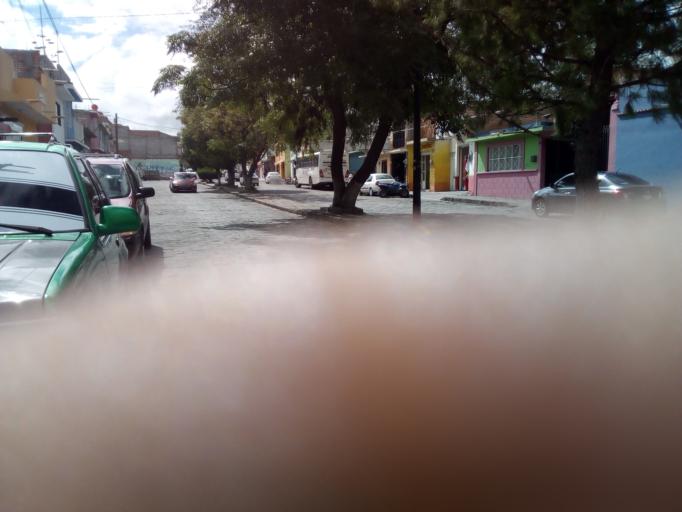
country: MX
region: Guerrero
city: San Luis de la Paz
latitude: 21.2957
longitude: -100.5125
